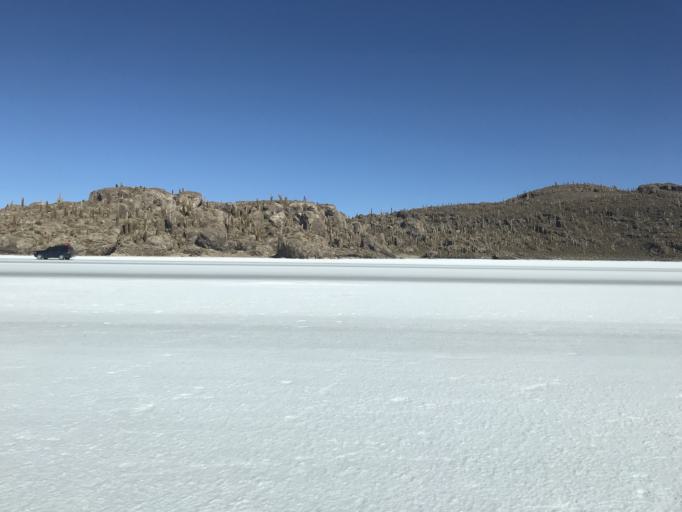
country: BO
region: Potosi
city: Colchani
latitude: -20.2382
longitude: -67.6238
